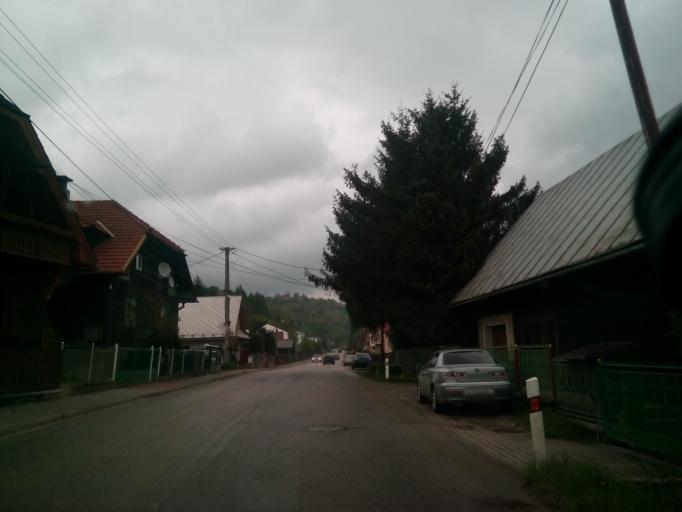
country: SK
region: Zilinsky
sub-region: Okres Zilina
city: Terchova
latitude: 49.2577
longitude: 19.0514
